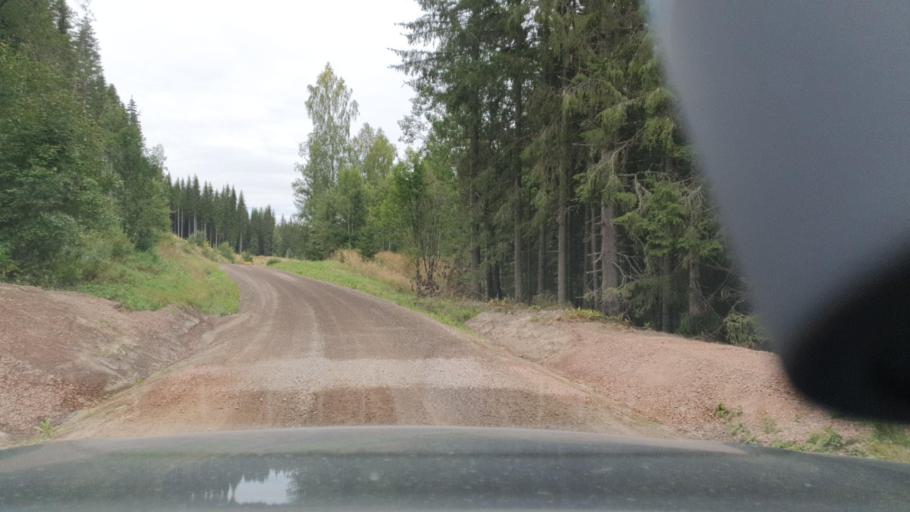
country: SE
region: Vaermland
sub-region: Eda Kommun
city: Charlottenberg
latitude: 60.0295
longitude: 12.6060
